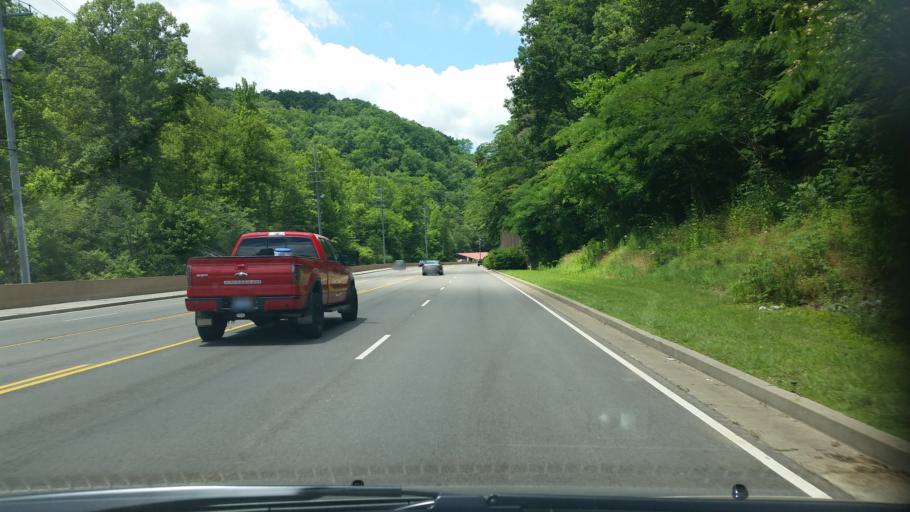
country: US
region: Tennessee
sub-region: Sevier County
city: Gatlinburg
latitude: 35.7274
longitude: -83.4619
